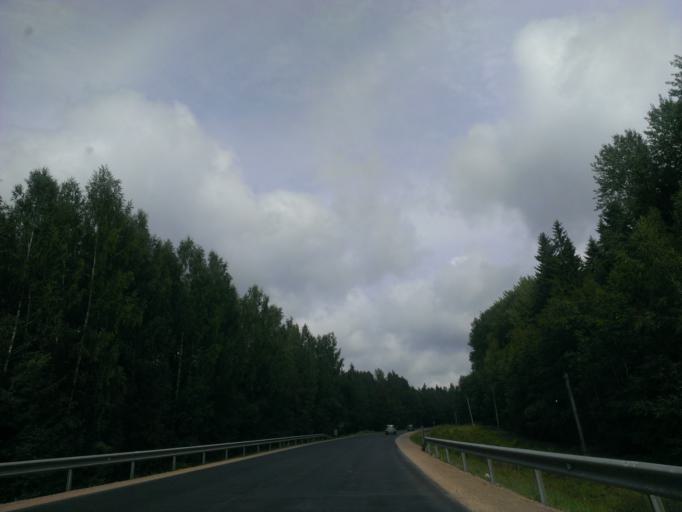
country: LV
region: Amatas Novads
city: Drabesi
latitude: 57.2120
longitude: 25.1764
